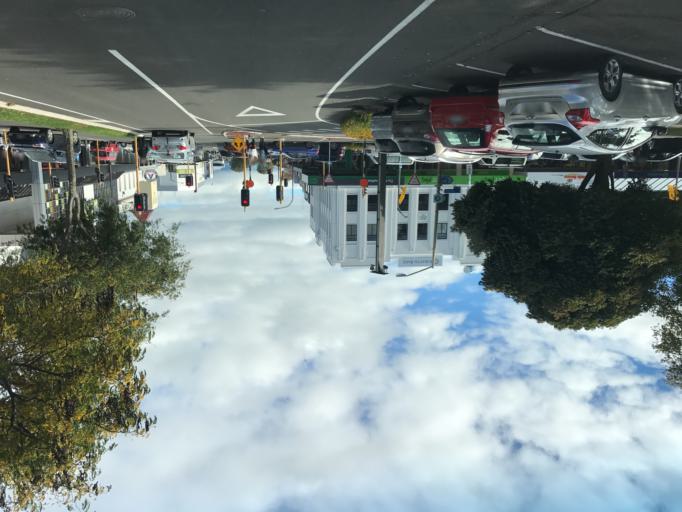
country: NZ
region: Manawatu-Wanganui
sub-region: Palmerston North City
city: Palmerston North
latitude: -40.3570
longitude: 175.6125
